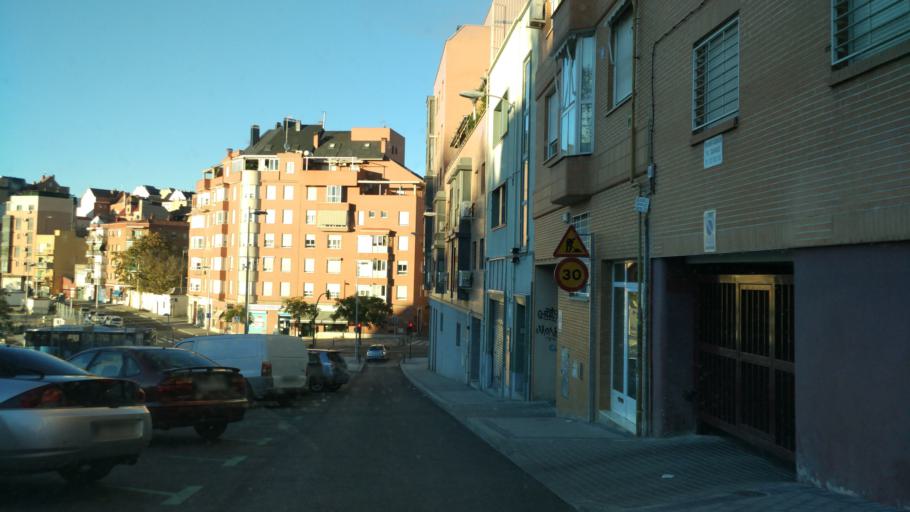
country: ES
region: Madrid
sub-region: Provincia de Madrid
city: Tetuan de las Victorias
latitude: 40.4632
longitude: -3.7053
